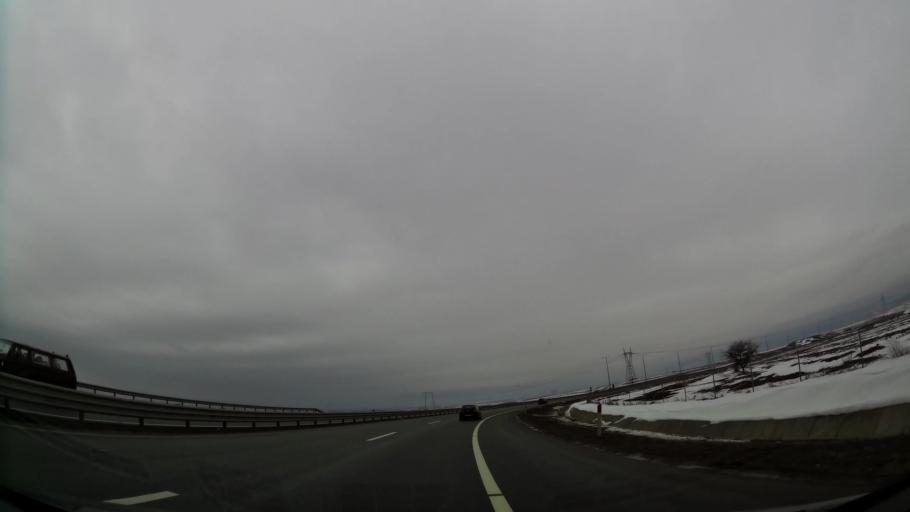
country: XK
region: Pristina
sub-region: Kosovo Polje
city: Kosovo Polje
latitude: 42.6203
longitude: 21.1267
